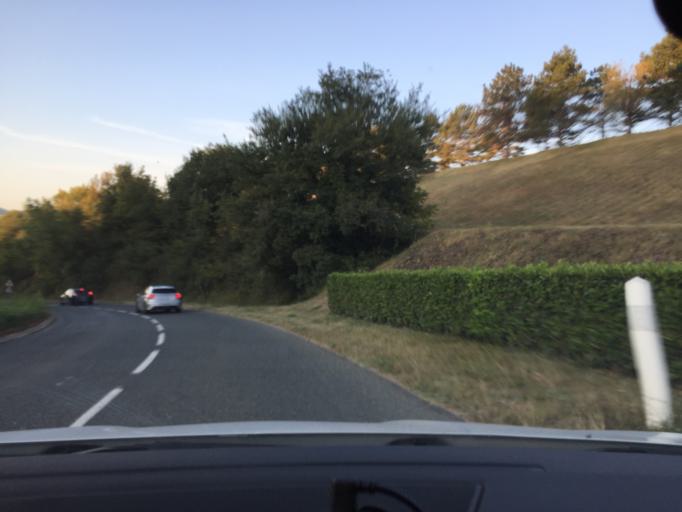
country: FR
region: Rhone-Alpes
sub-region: Departement du Rhone
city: Lozanne
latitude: 45.8625
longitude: 4.6683
